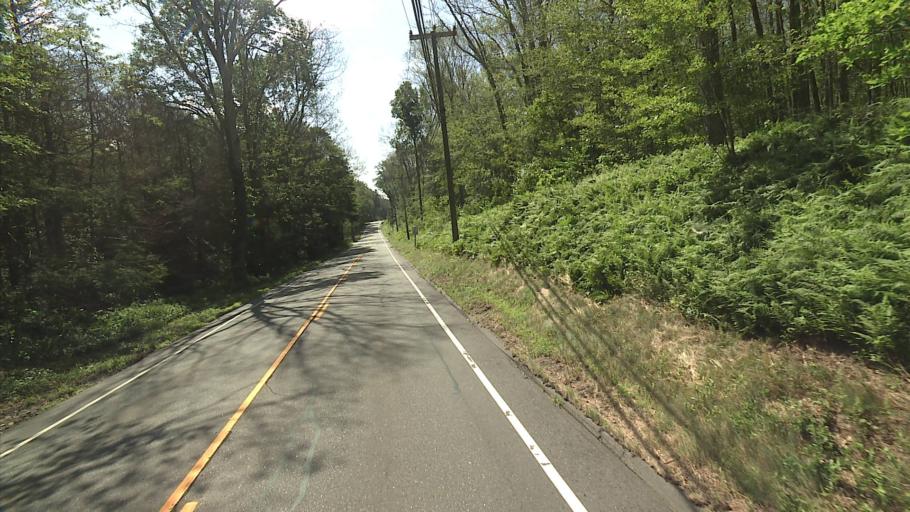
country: US
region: Connecticut
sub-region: Windham County
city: Plainfield Village
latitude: 41.7030
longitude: -72.0072
